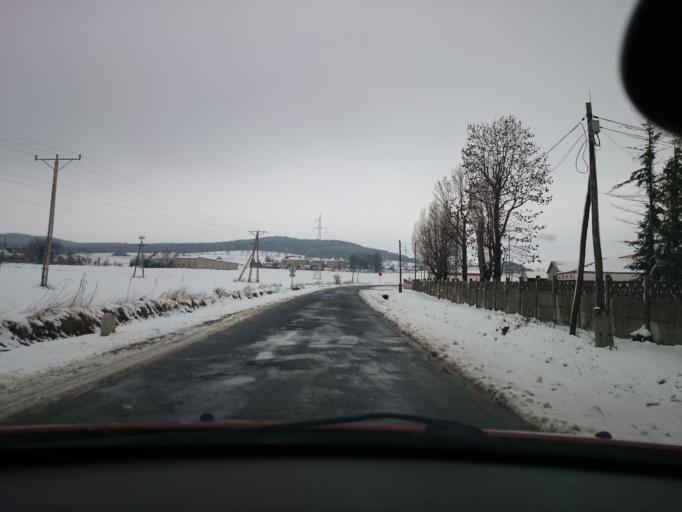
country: PL
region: Lower Silesian Voivodeship
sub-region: Powiat zabkowicki
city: Bardo
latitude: 50.5455
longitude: 16.7530
